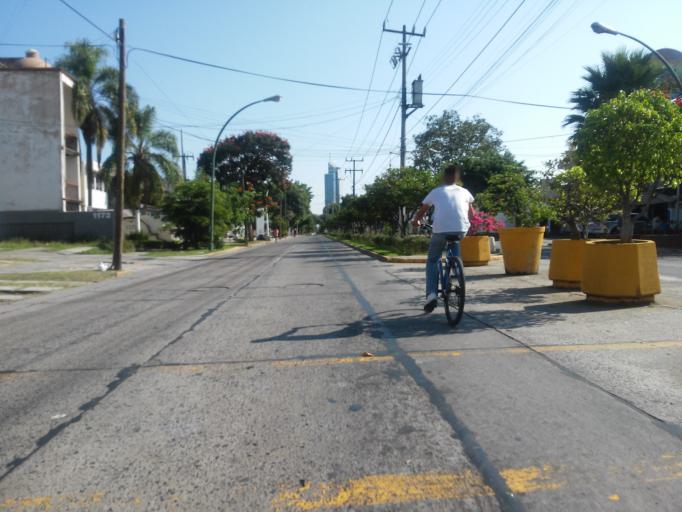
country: MX
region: Jalisco
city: Guadalajara
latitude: 20.6616
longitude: -103.4065
